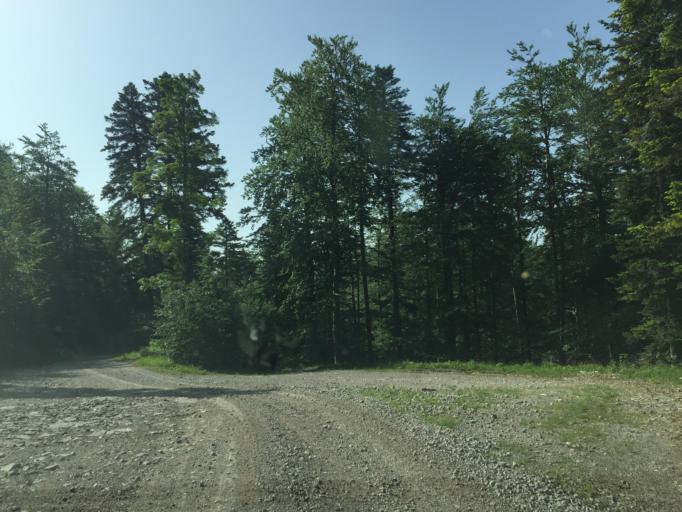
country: HR
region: Primorsko-Goranska
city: Podhum
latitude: 45.4599
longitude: 14.5394
